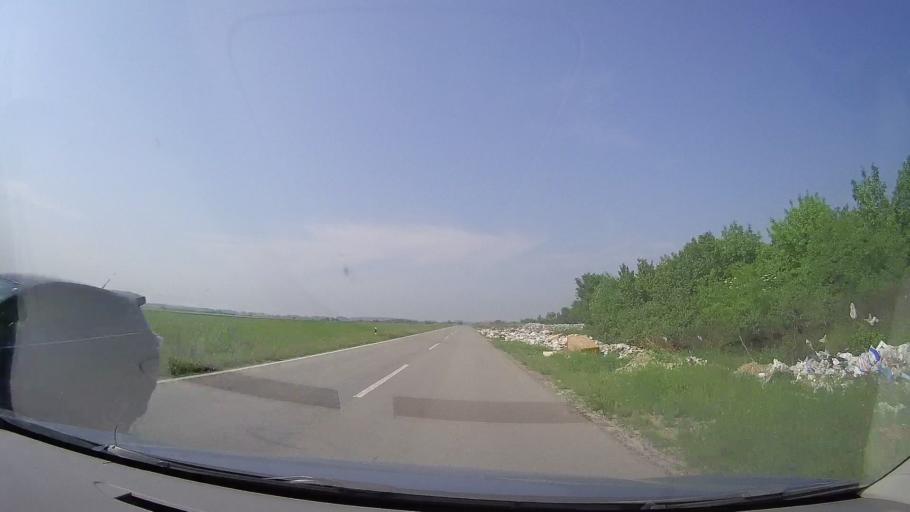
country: RS
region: Autonomna Pokrajina Vojvodina
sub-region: Srednjebanatski Okrug
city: Secanj
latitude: 45.3914
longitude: 20.8036
